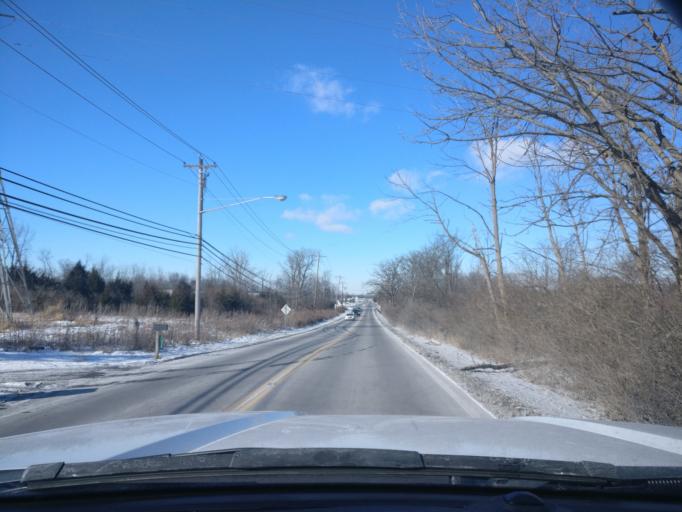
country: US
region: Ohio
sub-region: Warren County
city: Franklin
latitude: 39.5335
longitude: -84.2851
